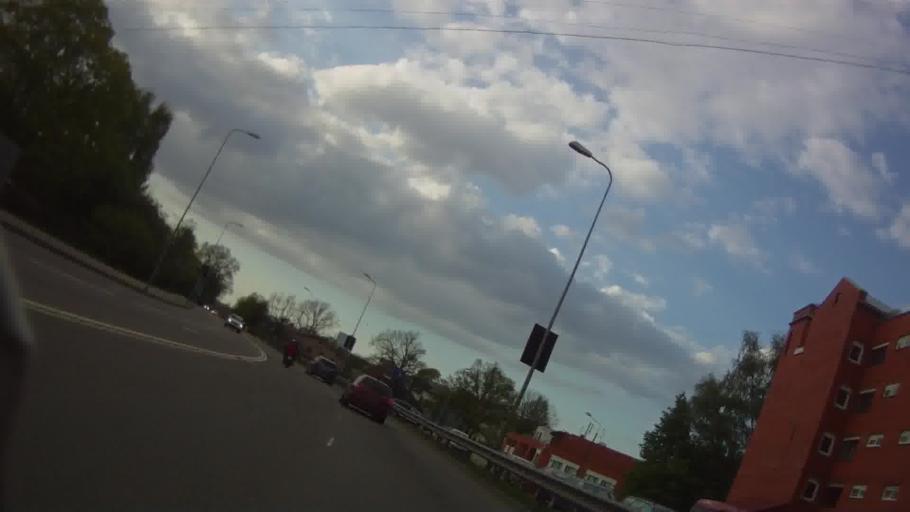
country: LV
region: Riga
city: Riga
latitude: 56.9687
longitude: 24.1697
